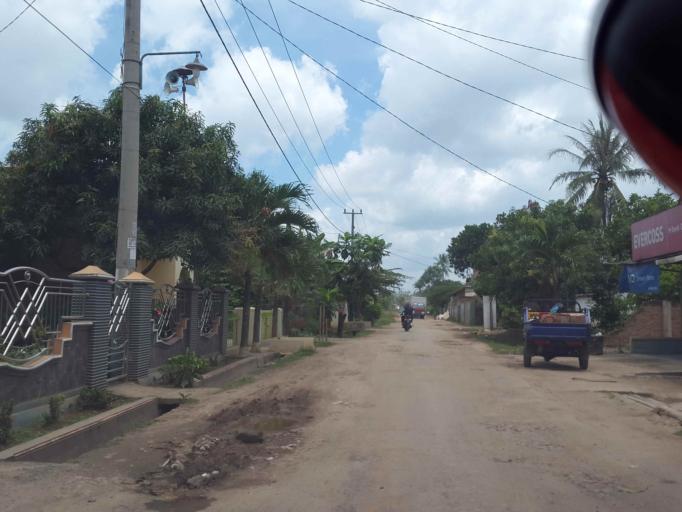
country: ID
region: Lampung
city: Natar
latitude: -5.3134
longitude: 105.2077
